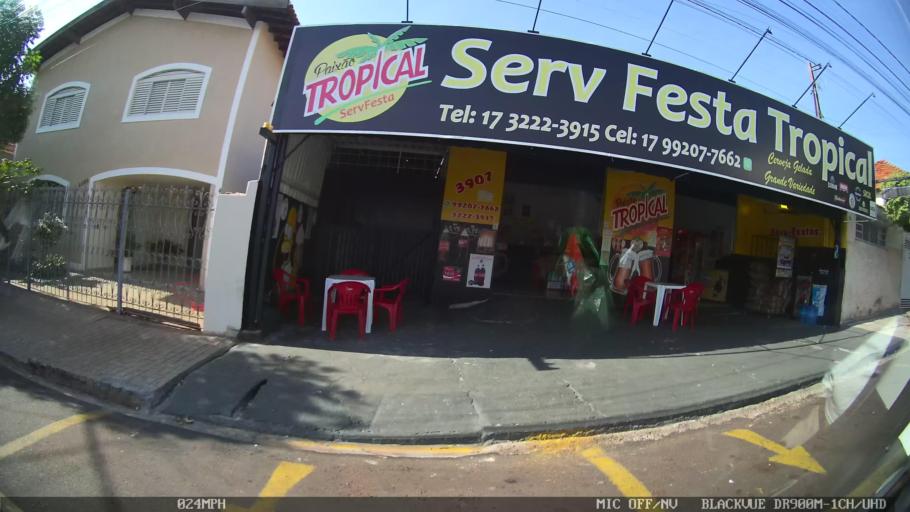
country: BR
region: Sao Paulo
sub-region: Sao Jose Do Rio Preto
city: Sao Jose do Rio Preto
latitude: -20.8214
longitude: -49.3784
